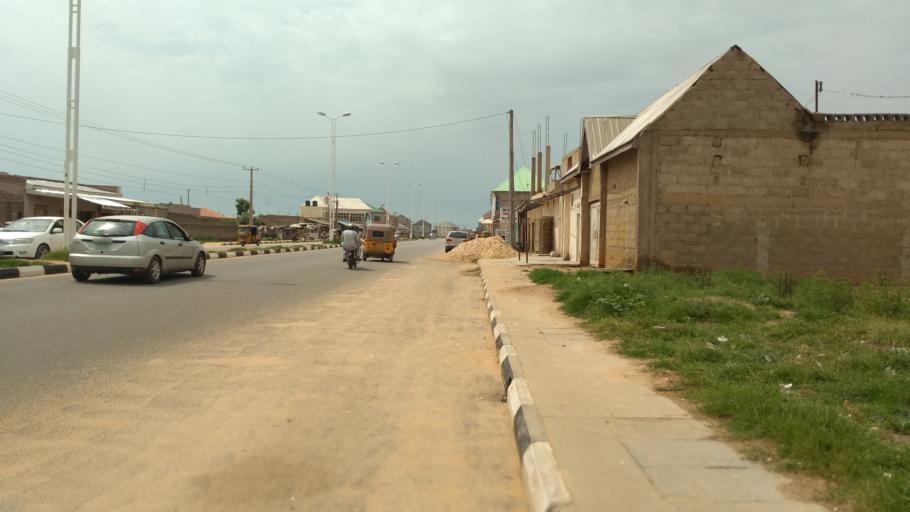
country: NG
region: Katsina
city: Katsina
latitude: 12.9773
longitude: 7.6417
